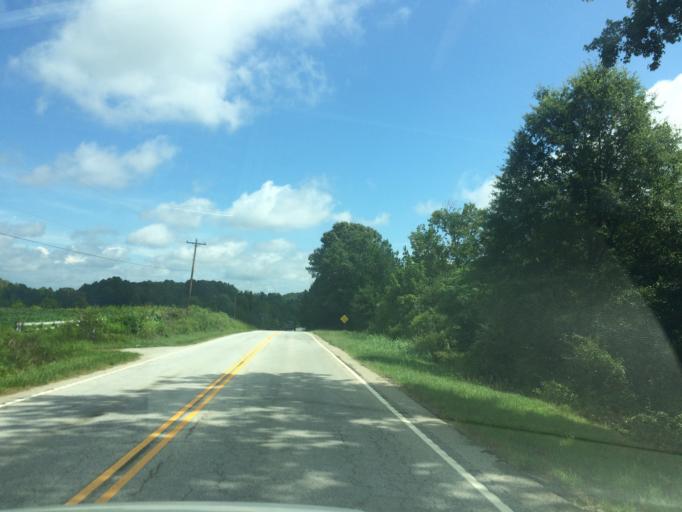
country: US
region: South Carolina
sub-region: Spartanburg County
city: Inman
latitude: 35.0651
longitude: -82.0794
